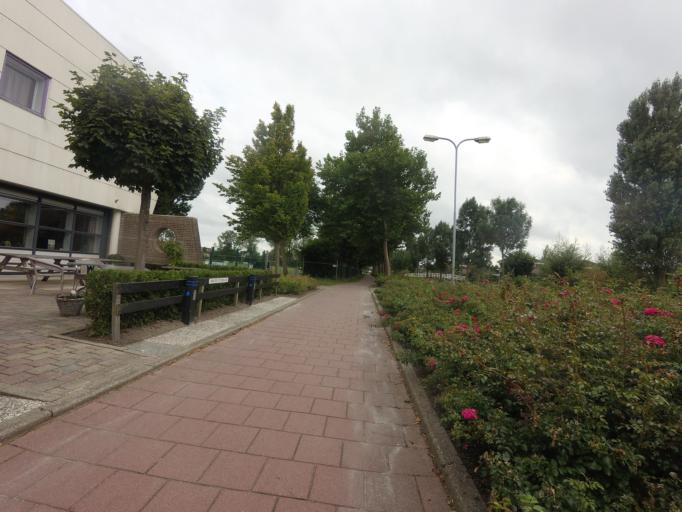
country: NL
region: North Holland
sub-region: Gemeente Medemblik
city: Opperdoes
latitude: 52.7221
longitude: 5.0758
